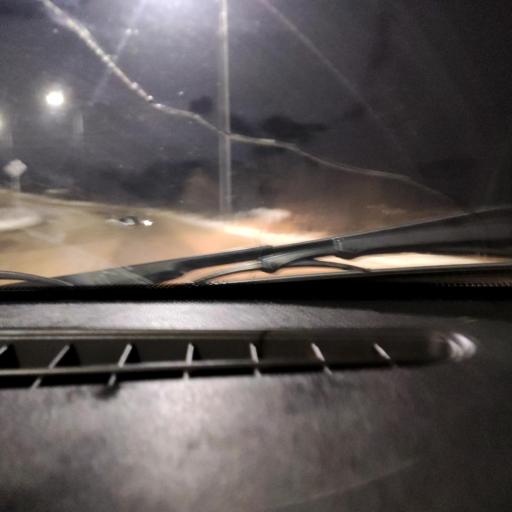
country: RU
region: Bashkortostan
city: Avdon
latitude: 54.6136
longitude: 55.8428
